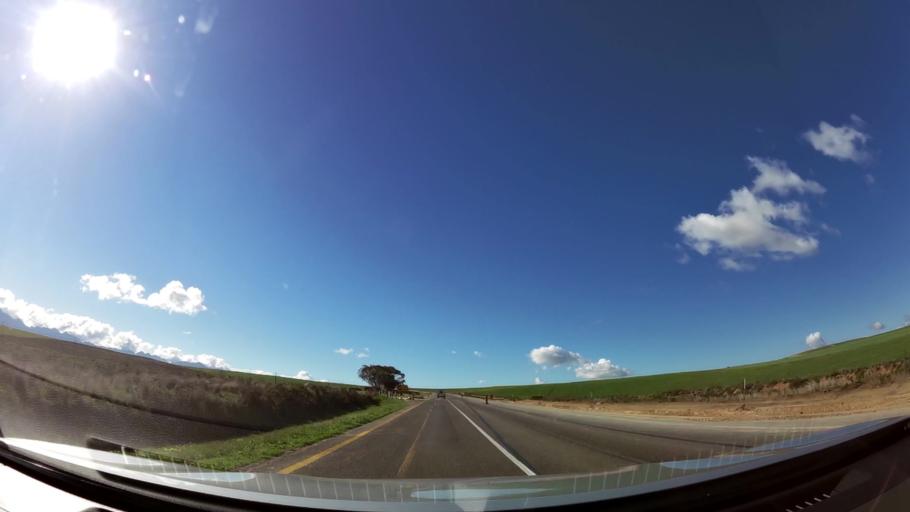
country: ZA
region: Western Cape
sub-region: Overberg District Municipality
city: Caledon
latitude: -34.1983
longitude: 19.6339
